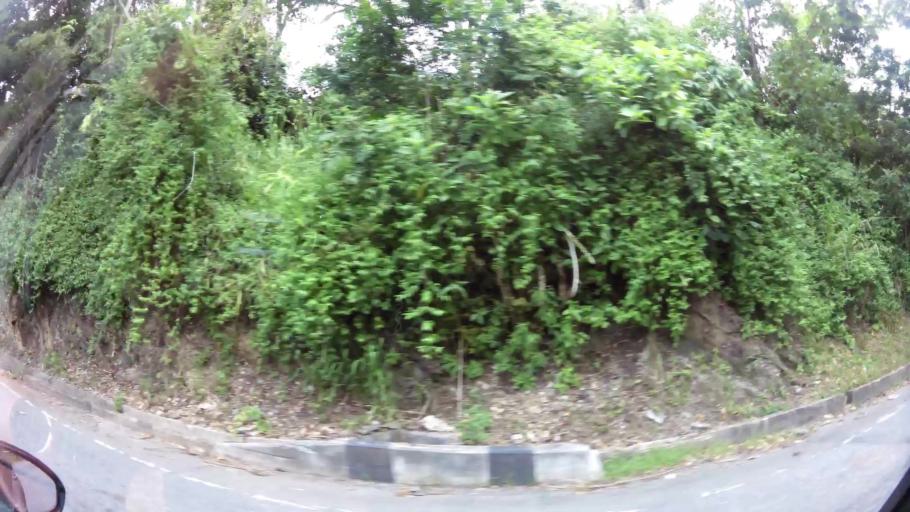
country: TT
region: Diego Martin
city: Petit Valley
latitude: 10.7332
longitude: -61.4921
